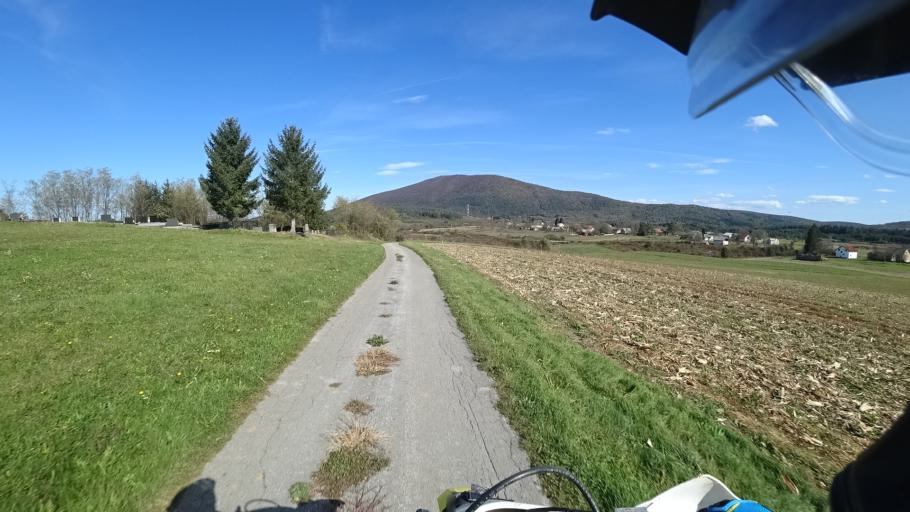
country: HR
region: Karlovacka
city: Plaski
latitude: 45.1127
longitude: 15.3578
